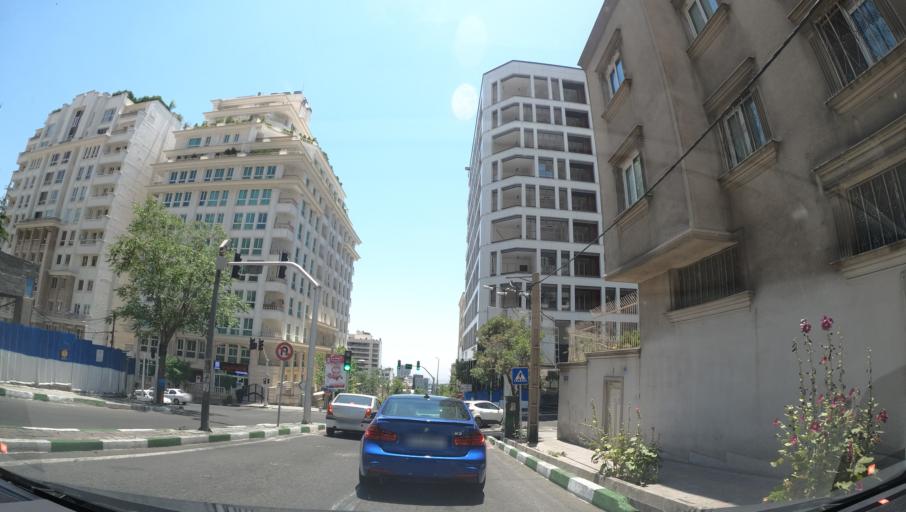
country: IR
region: Tehran
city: Tajrish
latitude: 35.8067
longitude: 51.4017
